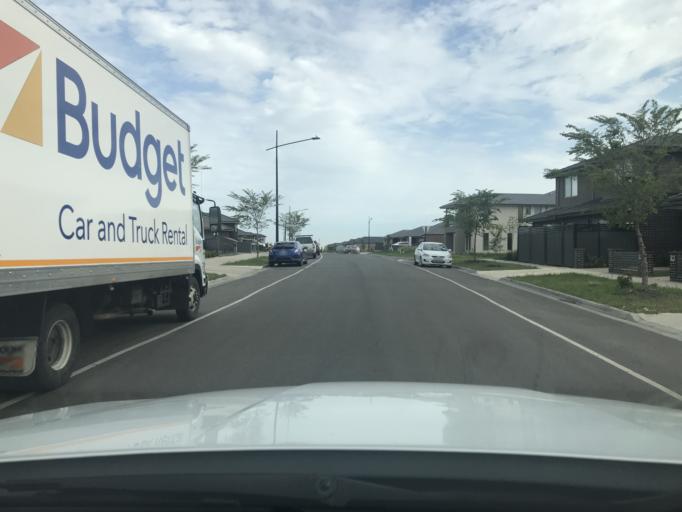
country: AU
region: Victoria
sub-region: Hume
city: Roxburgh Park
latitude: -37.6000
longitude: 144.8950
